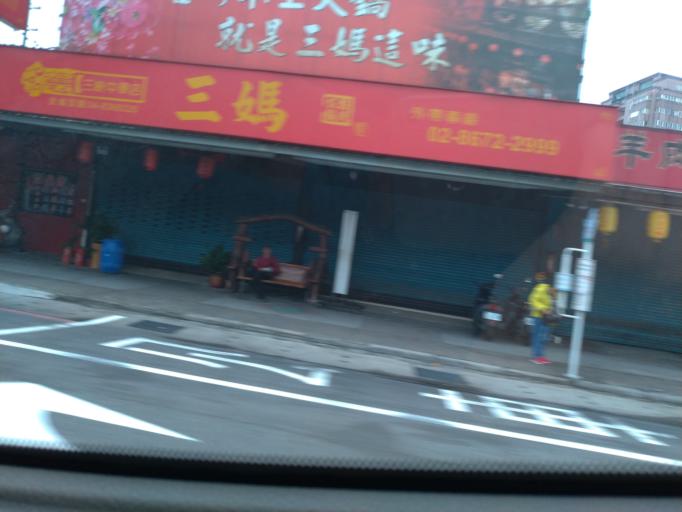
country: TW
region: Taiwan
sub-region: Taoyuan
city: Taoyuan
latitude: 24.9327
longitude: 121.3757
